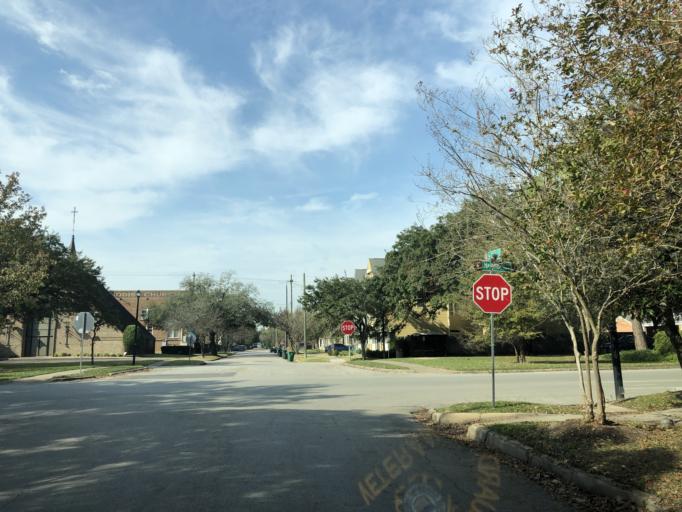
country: US
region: Texas
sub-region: Harris County
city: Houston
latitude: 29.7944
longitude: -95.3973
